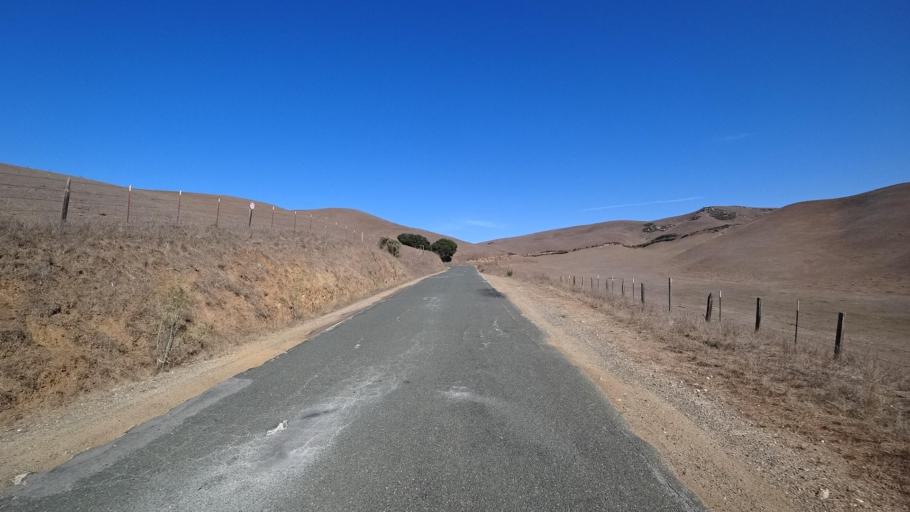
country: US
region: California
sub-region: San Benito County
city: San Juan Bautista
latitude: 36.8074
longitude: -121.5826
